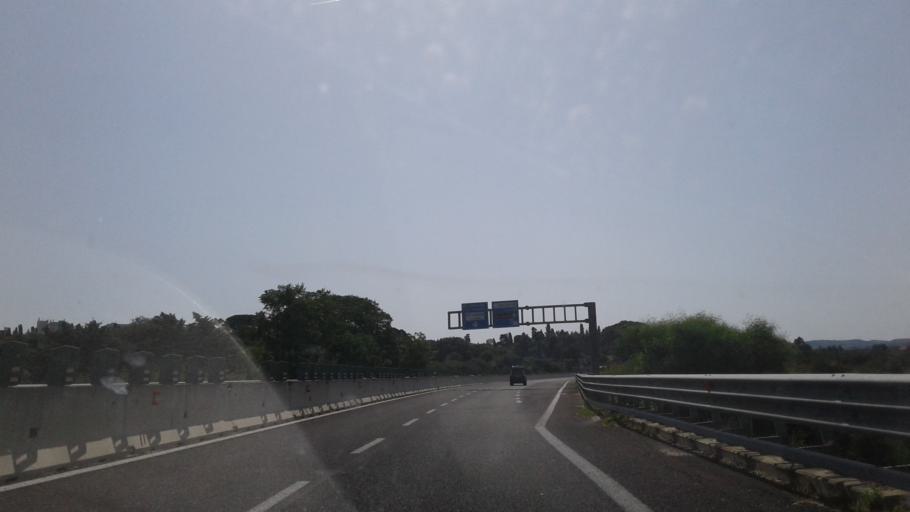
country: IT
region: Sardinia
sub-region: Provincia di Sassari
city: Sassari
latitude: 40.7113
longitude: 8.5440
